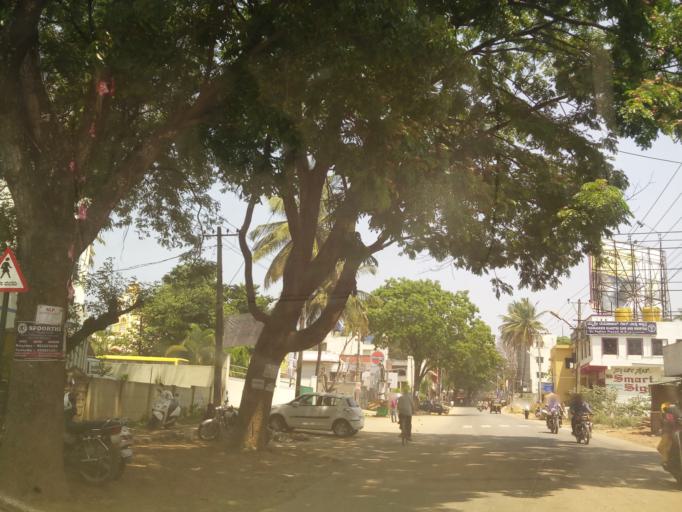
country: IN
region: Karnataka
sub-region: Hassan
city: Hassan
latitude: 13.0121
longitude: 76.0996
